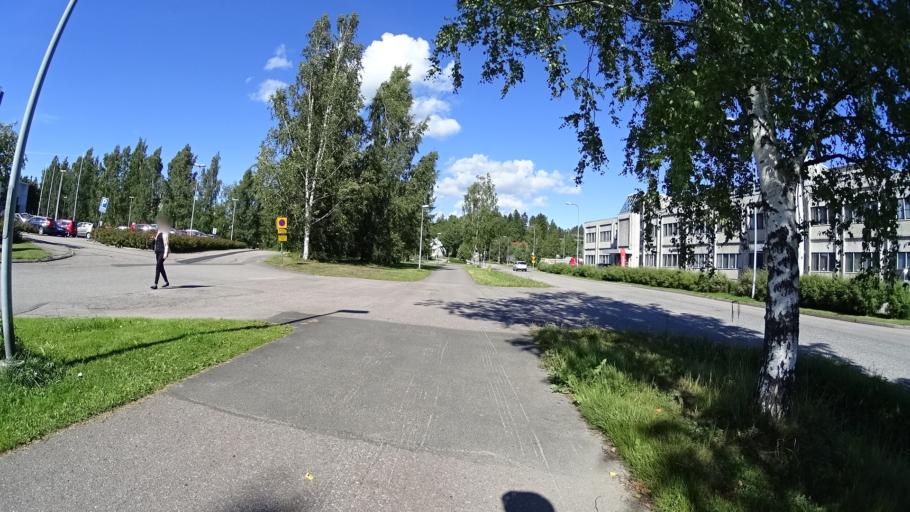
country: FI
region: Uusimaa
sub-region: Helsinki
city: Kilo
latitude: 60.2080
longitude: 24.7653
